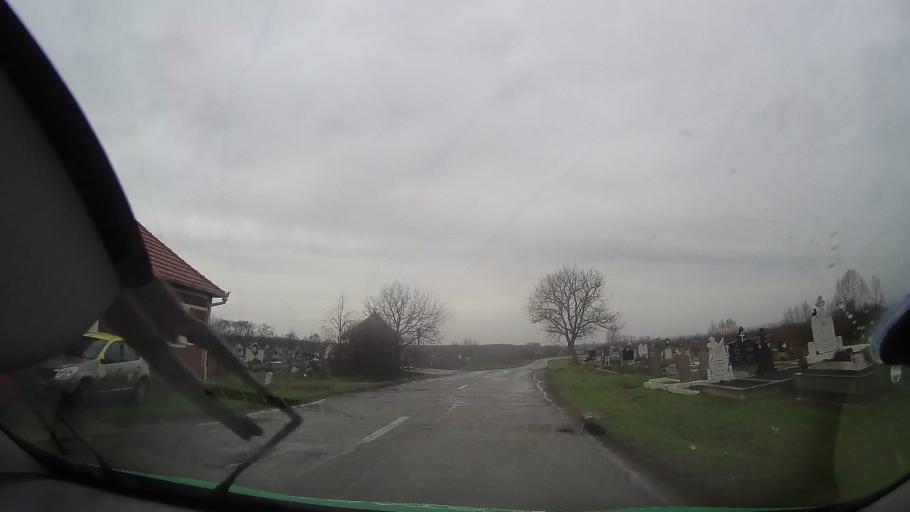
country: RO
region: Bihor
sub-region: Comuna Cociuba Mare
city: Cociuba Mare
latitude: 46.7383
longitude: 21.9910
